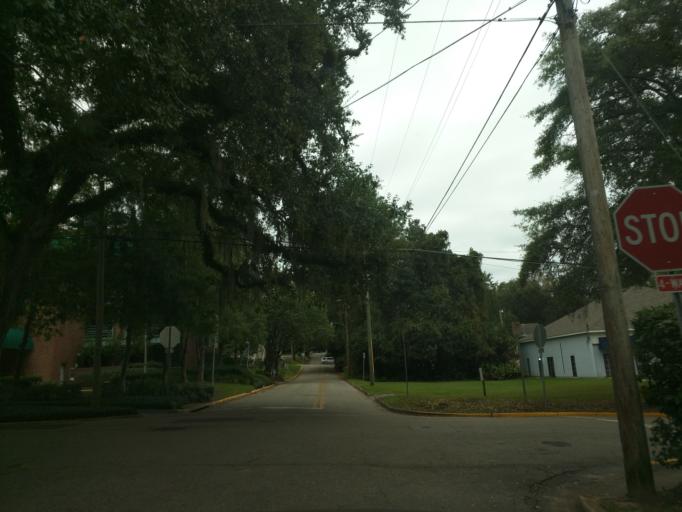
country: US
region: Florida
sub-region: Leon County
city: Tallahassee
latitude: 30.4395
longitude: -84.2771
